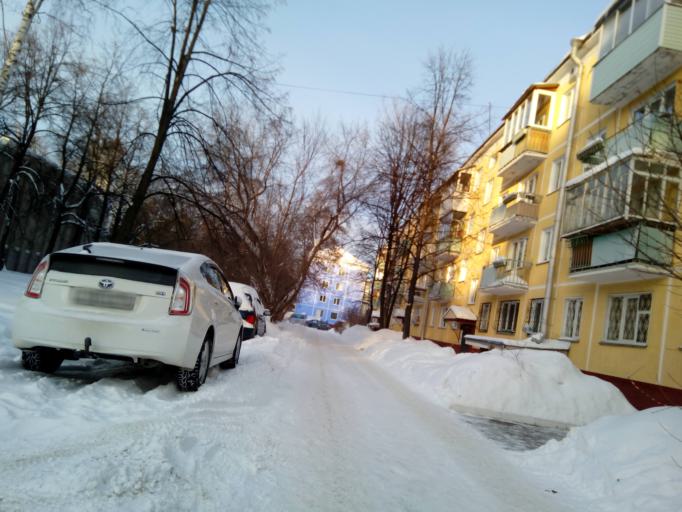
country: RU
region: Novosibirsk
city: Akademgorodok
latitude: 54.8359
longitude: 83.1070
